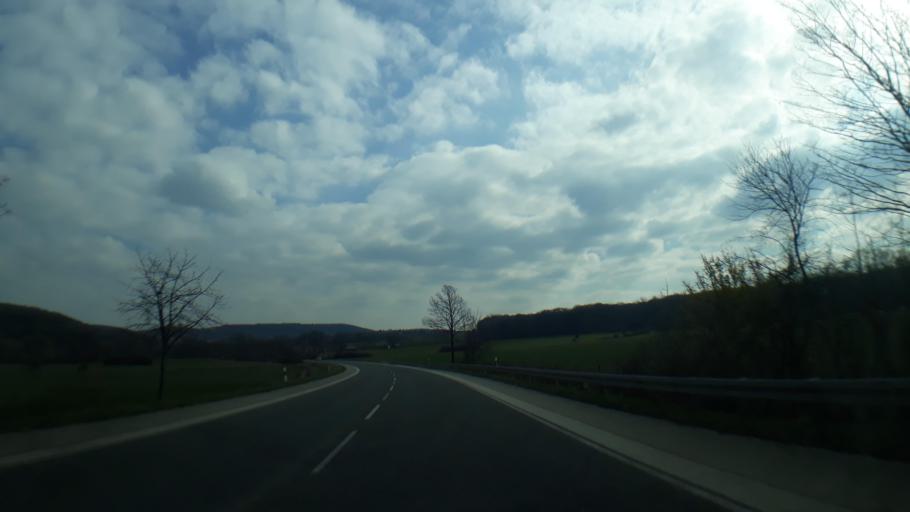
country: DE
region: North Rhine-Westphalia
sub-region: Regierungsbezirk Koln
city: Rheinbach
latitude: 50.6006
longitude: 6.8697
